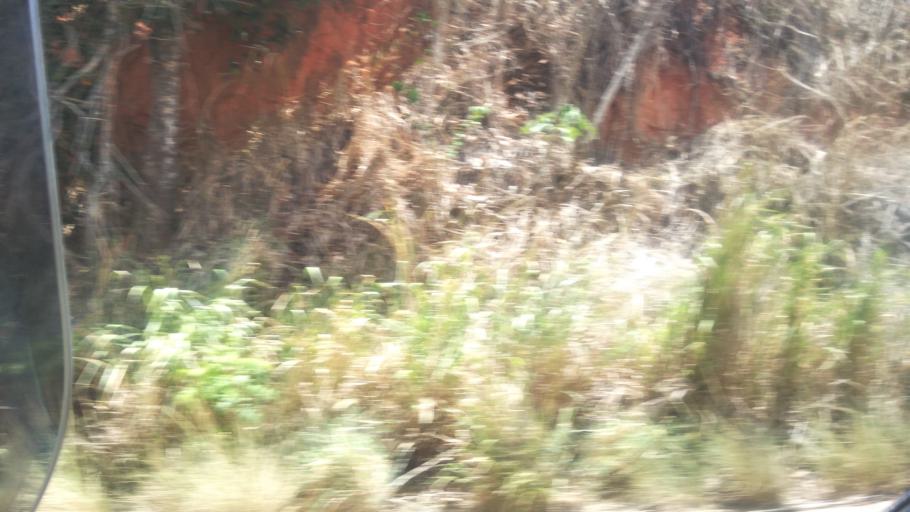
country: BR
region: Pernambuco
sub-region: Nazare Da Mata
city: Nazare da Mata
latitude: -7.7385
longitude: -35.2957
